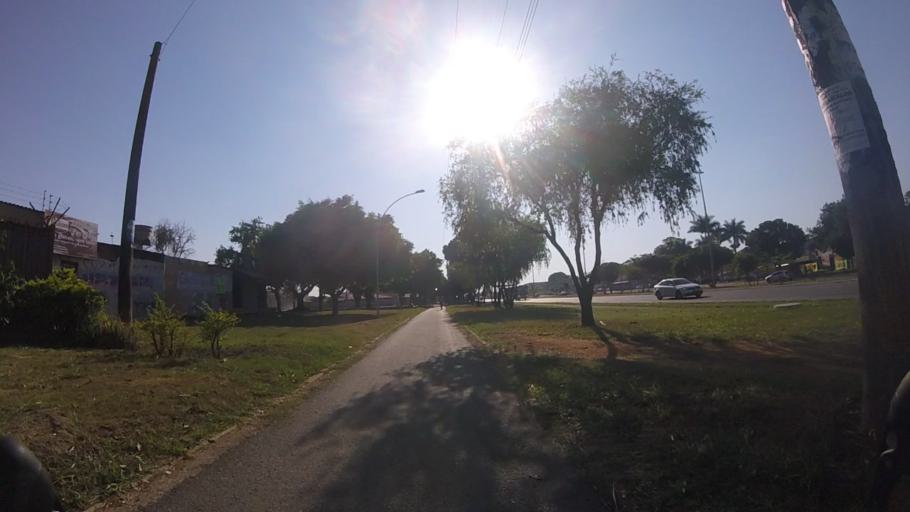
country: BR
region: Federal District
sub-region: Brasilia
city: Brasilia
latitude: -15.8462
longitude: -47.9740
